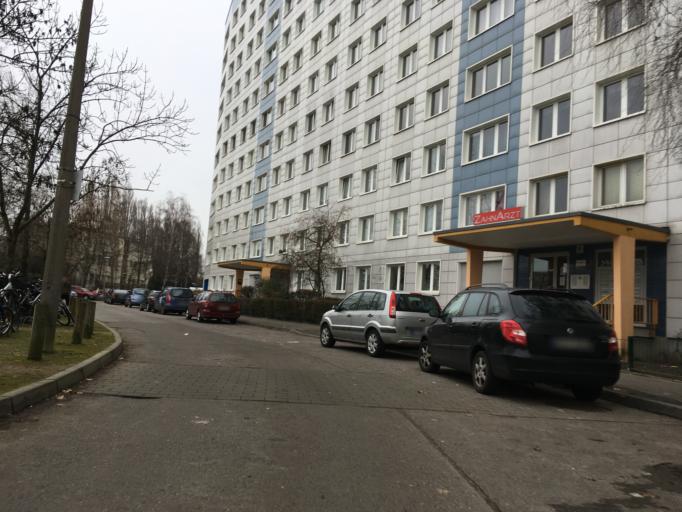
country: DE
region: Berlin
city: Rummelsburg
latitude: 52.5105
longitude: 13.4876
